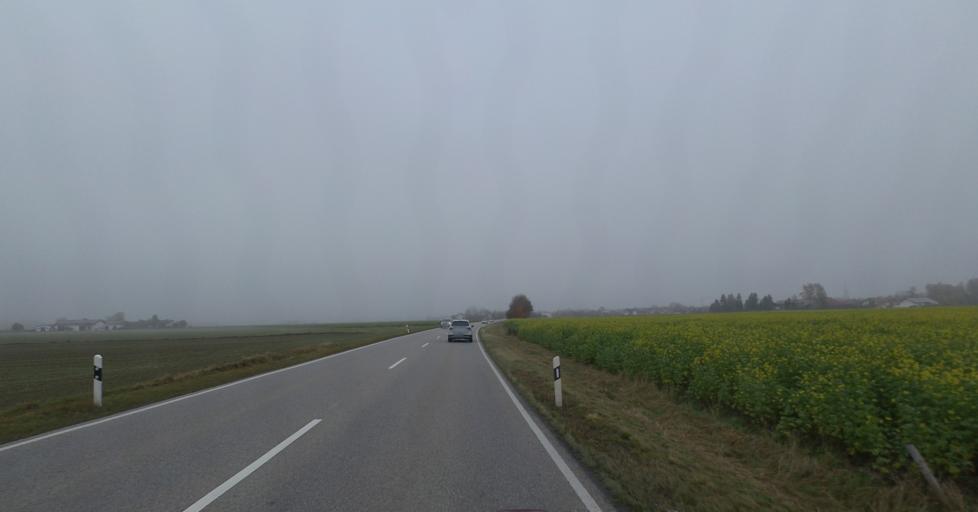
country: DE
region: Bavaria
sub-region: Upper Bavaria
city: Unterneukirchen
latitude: 48.1601
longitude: 12.6109
